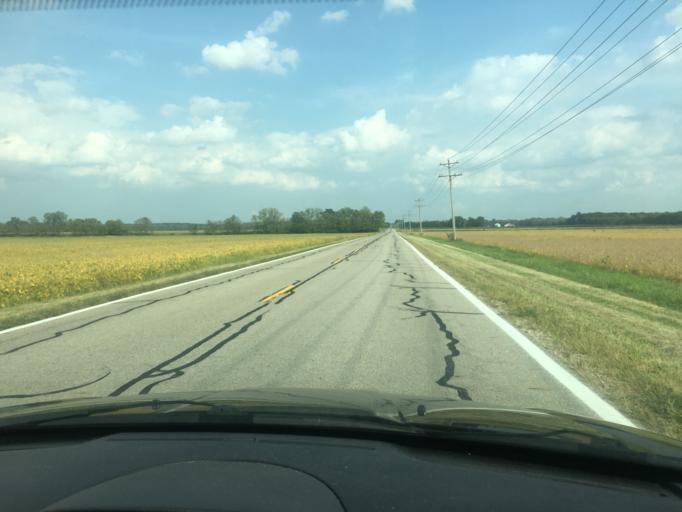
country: US
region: Ohio
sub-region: Champaign County
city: Urbana
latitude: 40.1313
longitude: -83.8313
